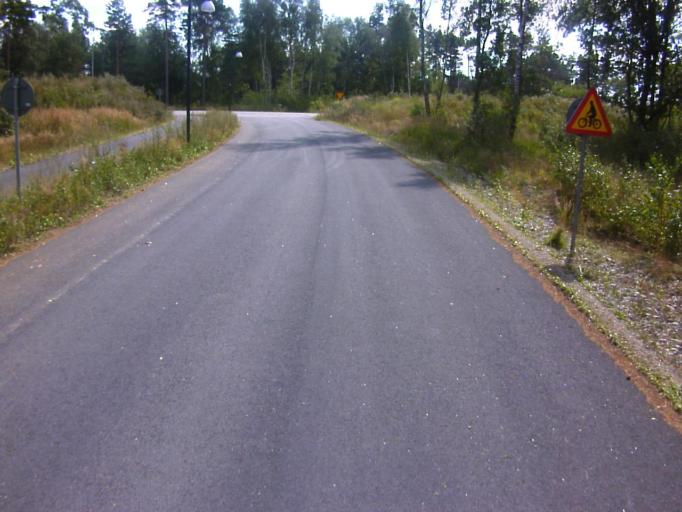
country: SE
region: Blekinge
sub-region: Solvesborgs Kommun
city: Soelvesborg
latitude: 56.0510
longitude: 14.6103
